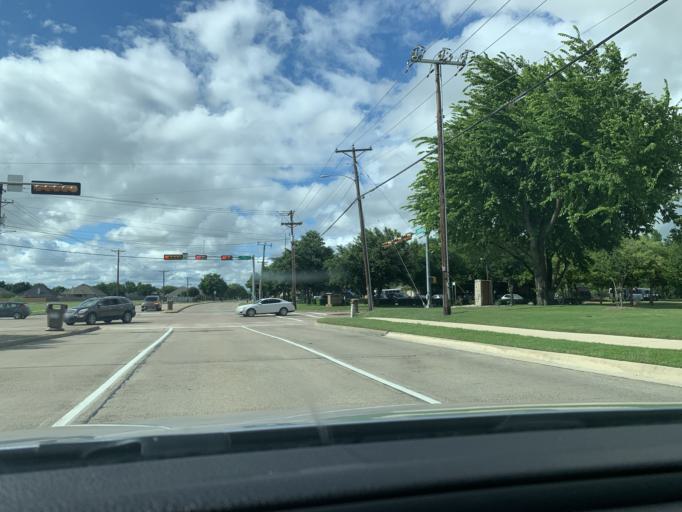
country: US
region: Texas
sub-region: Dallas County
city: Grand Prairie
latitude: 32.6579
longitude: -97.0152
